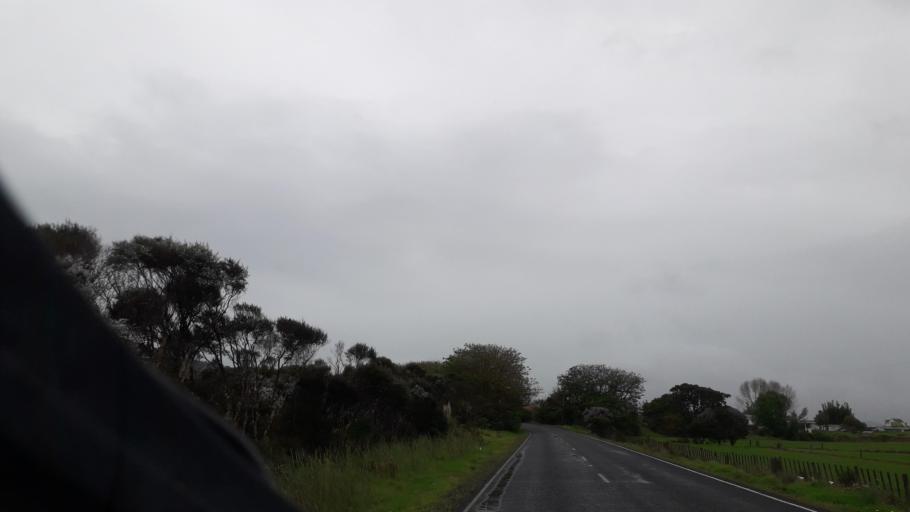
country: NZ
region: Northland
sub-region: Far North District
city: Kaitaia
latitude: -35.3693
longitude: 173.4989
